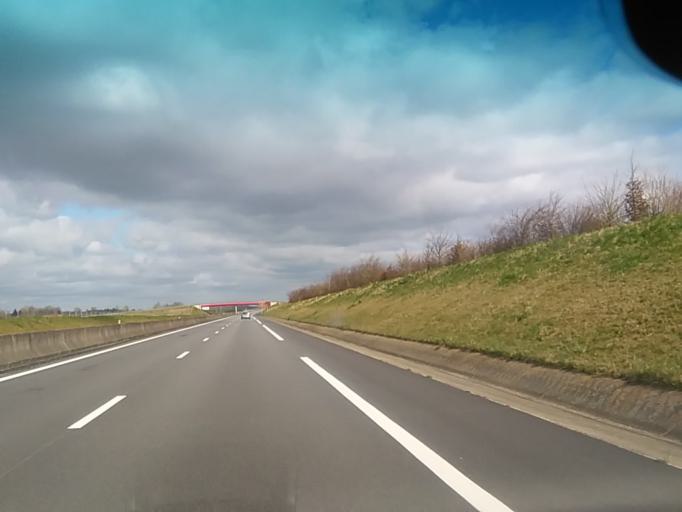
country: FR
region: Haute-Normandie
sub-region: Departement de l'Eure
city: Thiberville
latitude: 49.0686
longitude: 0.4703
